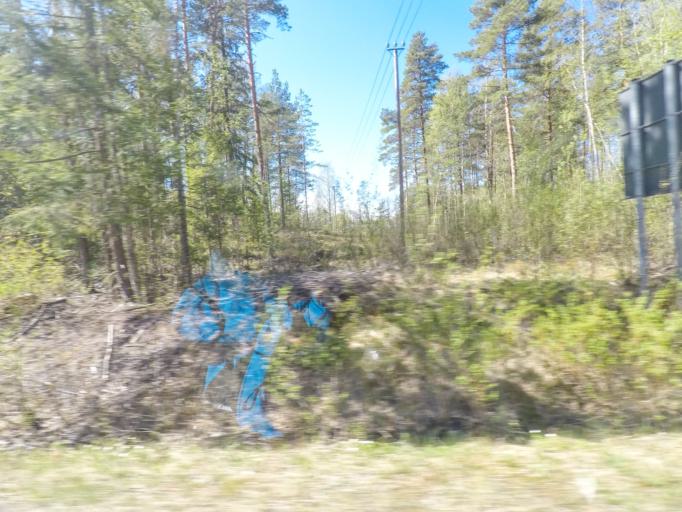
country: FI
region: Uusimaa
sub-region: Helsinki
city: Sammatti
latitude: 60.3550
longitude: 23.8017
